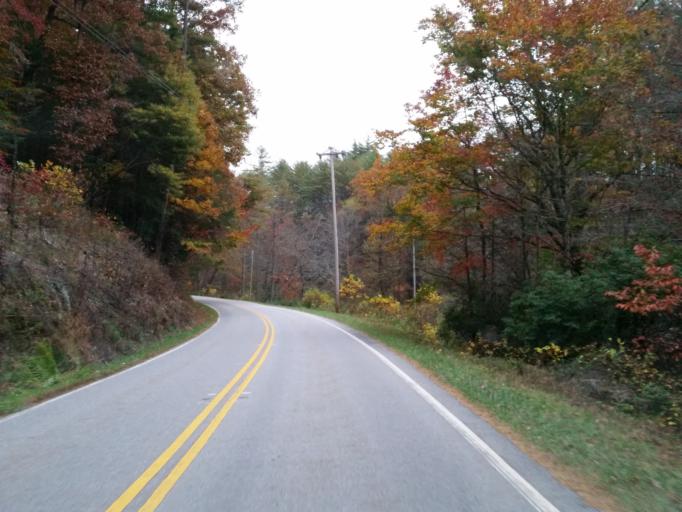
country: US
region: Georgia
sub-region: Union County
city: Blairsville
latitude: 34.7386
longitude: -84.0835
